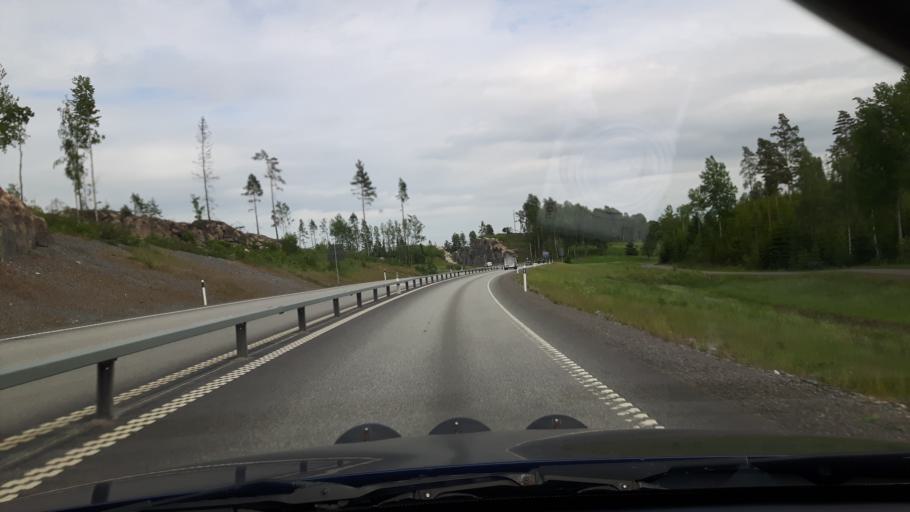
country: SE
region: Soedermanland
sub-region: Flens Kommun
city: Malmkoping
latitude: 59.1288
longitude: 16.6751
